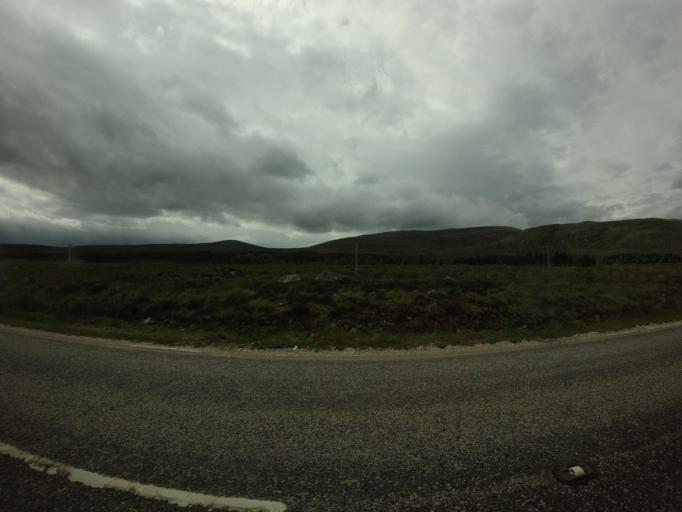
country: GB
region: Scotland
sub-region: Highland
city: Ullapool
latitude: 57.7129
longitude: -4.8463
